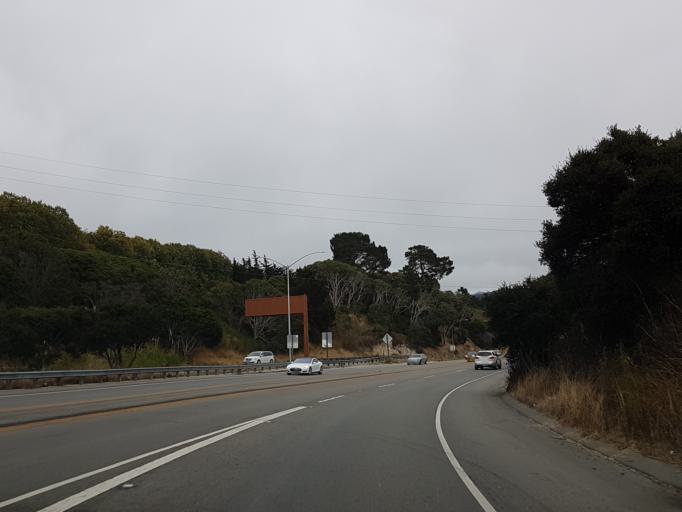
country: US
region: California
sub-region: Monterey County
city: Seaside
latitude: 36.5939
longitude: -121.8675
